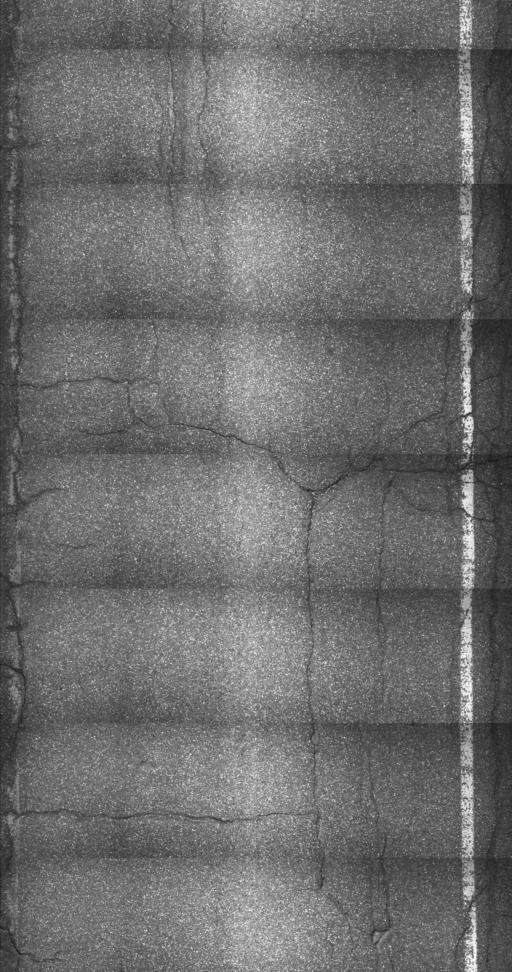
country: US
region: Vermont
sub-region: Caledonia County
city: Hardwick
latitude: 44.3778
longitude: -72.4184
